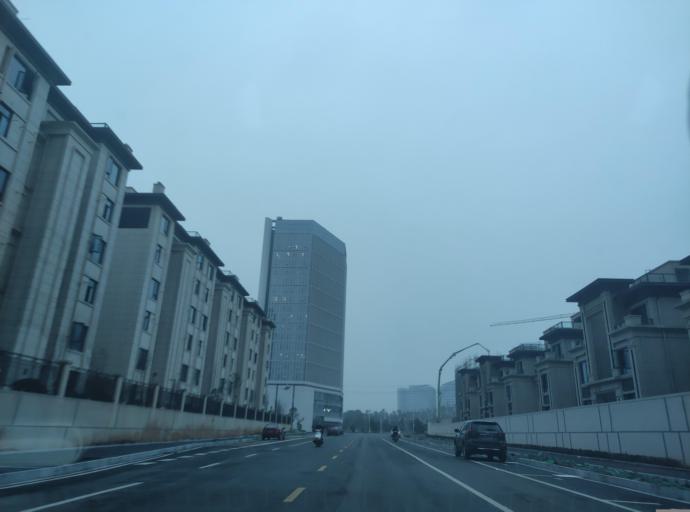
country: CN
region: Jiangxi Sheng
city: Pingxiang
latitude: 27.6661
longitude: 113.8863
